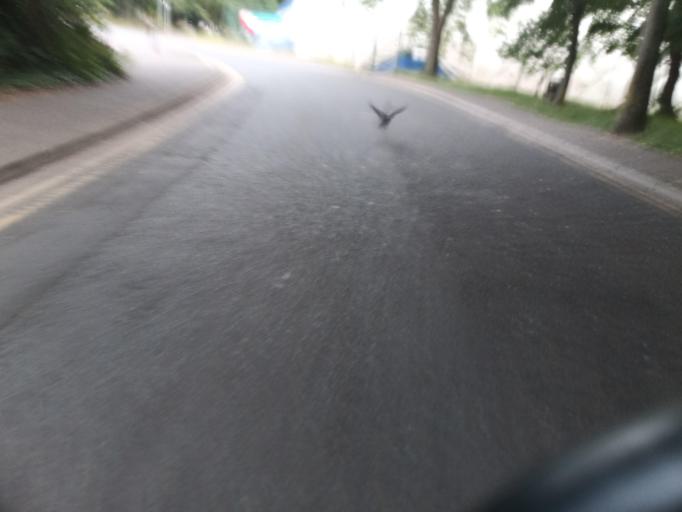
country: GB
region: Northern Ireland
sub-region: Ards District
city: Comber
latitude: 54.5515
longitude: -5.7444
